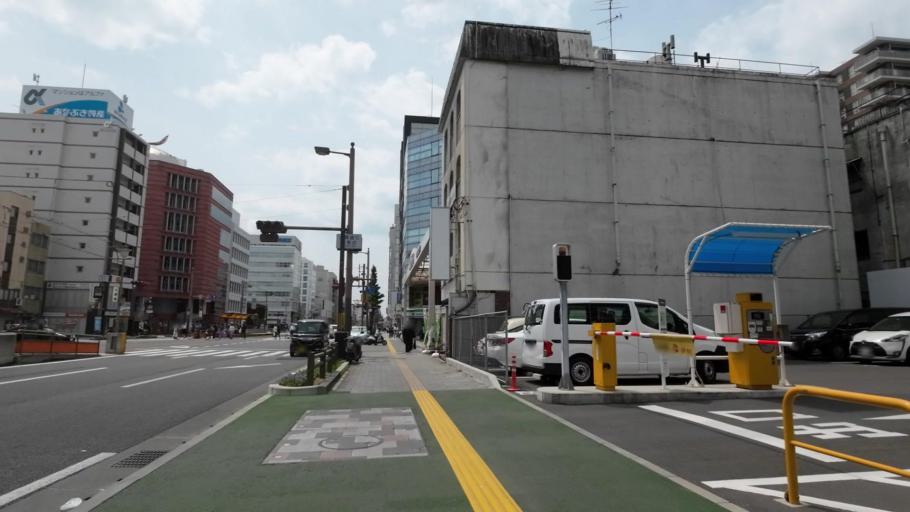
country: JP
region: Kochi
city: Kochi-shi
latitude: 33.5592
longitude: 133.5368
